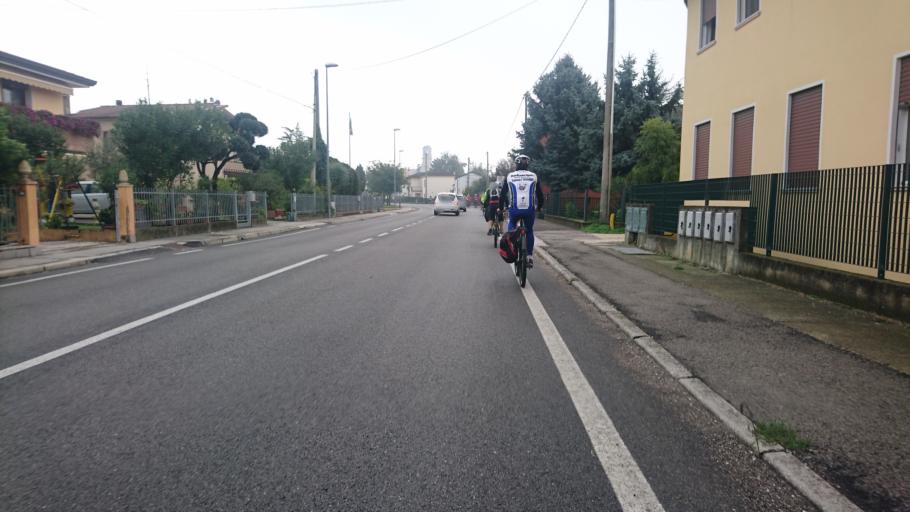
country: IT
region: Veneto
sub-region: Provincia di Padova
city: Pozzonovo
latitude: 45.1991
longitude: 11.7869
